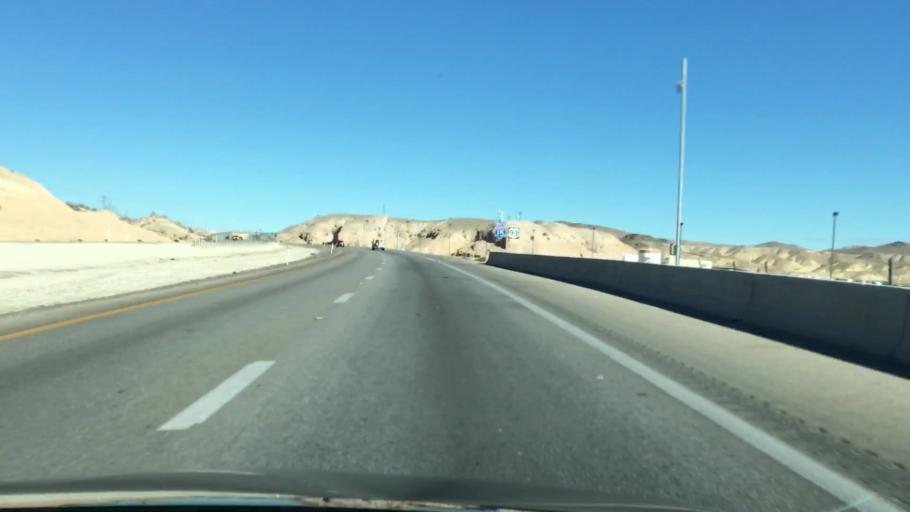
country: US
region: Nevada
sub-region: Clark County
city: Nellis Air Force Base
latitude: 36.3132
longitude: -114.9453
